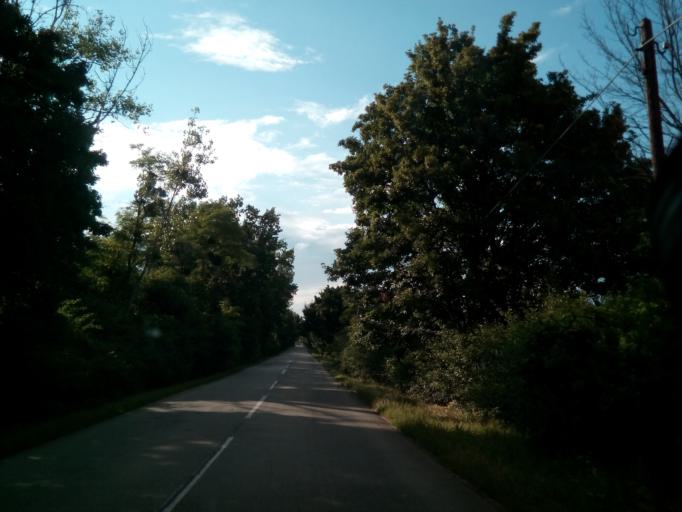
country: SK
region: Kosicky
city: Secovce
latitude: 48.5940
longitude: 21.5605
